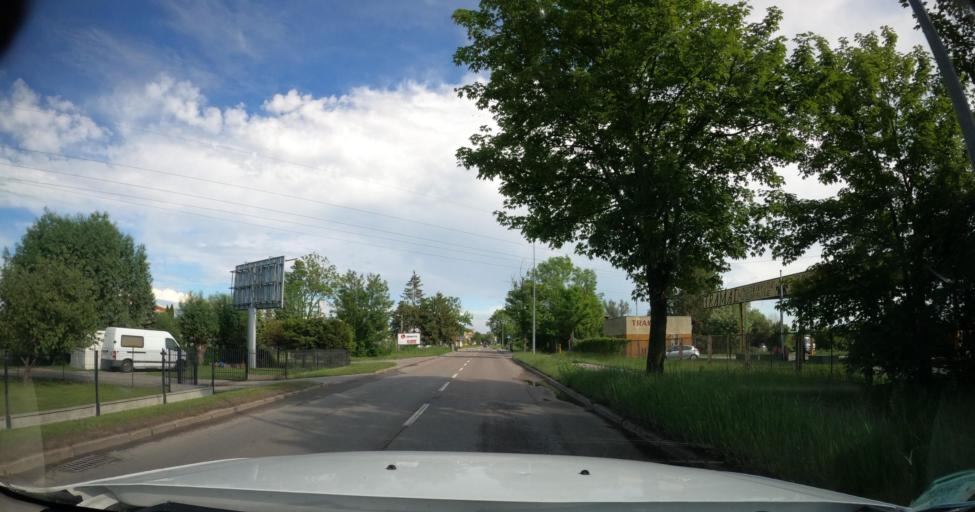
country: PL
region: Warmian-Masurian Voivodeship
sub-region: Powiat elblaski
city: Elblag
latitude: 54.1636
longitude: 19.3799
